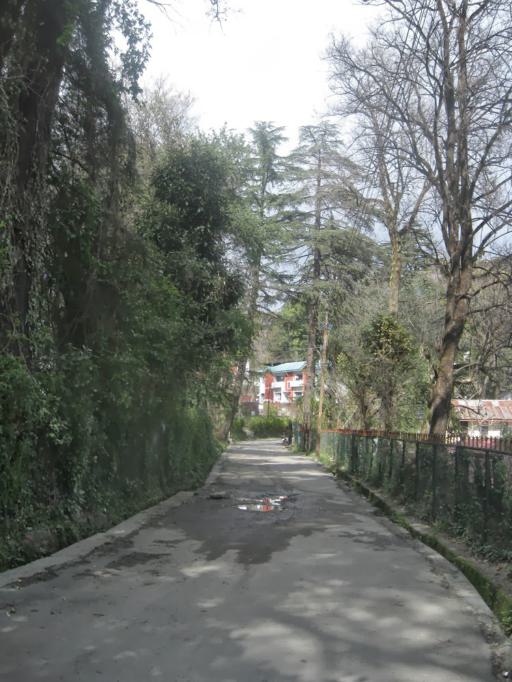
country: IN
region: Himachal Pradesh
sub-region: Kangra
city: Palampur
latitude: 32.1154
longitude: 76.5383
